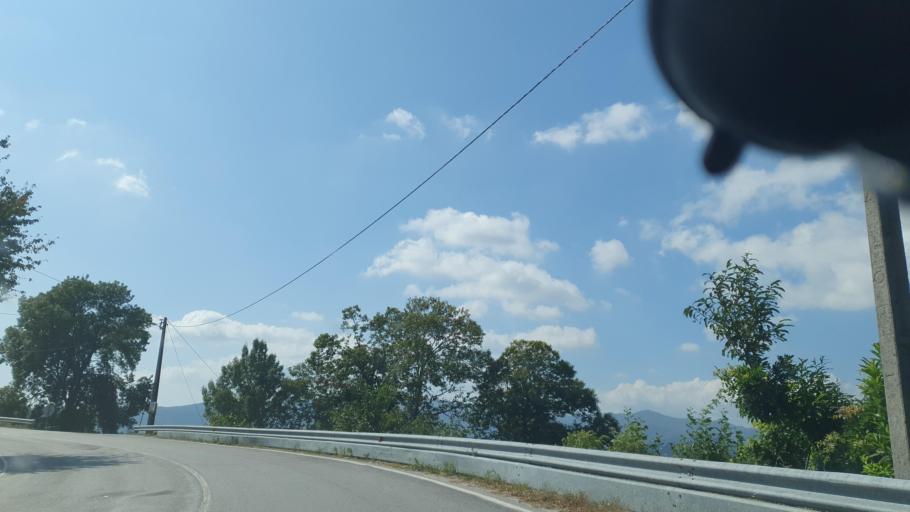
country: PT
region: Braga
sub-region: Vieira do Minho
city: Vieira do Minho
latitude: 41.6740
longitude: -8.1467
